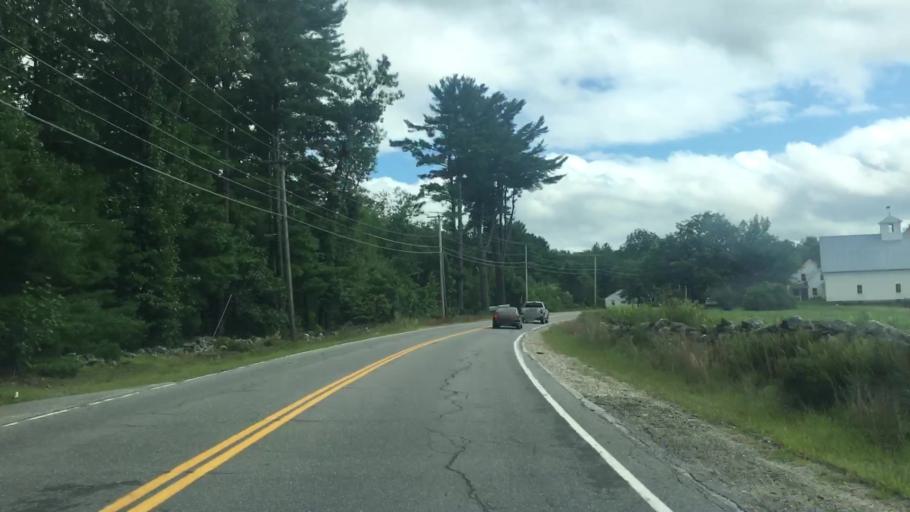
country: US
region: Maine
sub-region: York County
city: Lake Arrowhead
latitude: 43.6087
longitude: -70.7156
